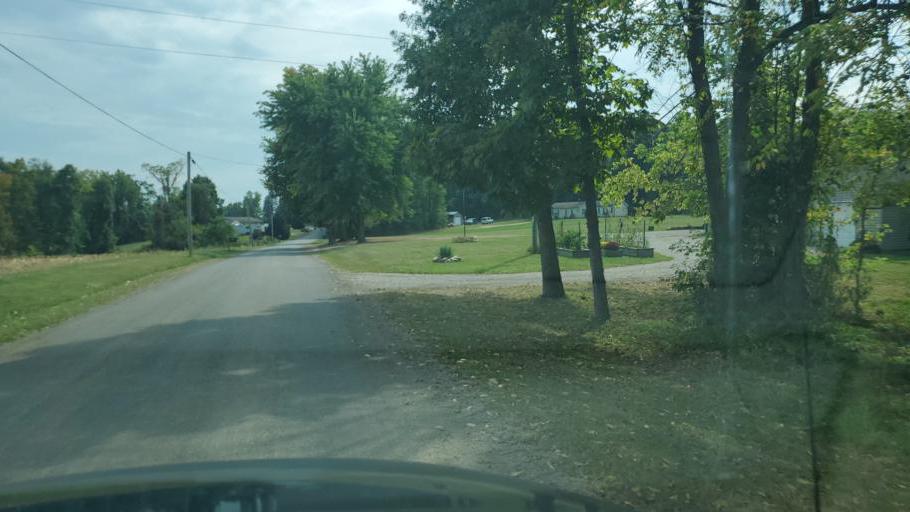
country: US
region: Ohio
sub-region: Muskingum County
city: Frazeysburg
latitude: 40.0011
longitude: -82.1903
